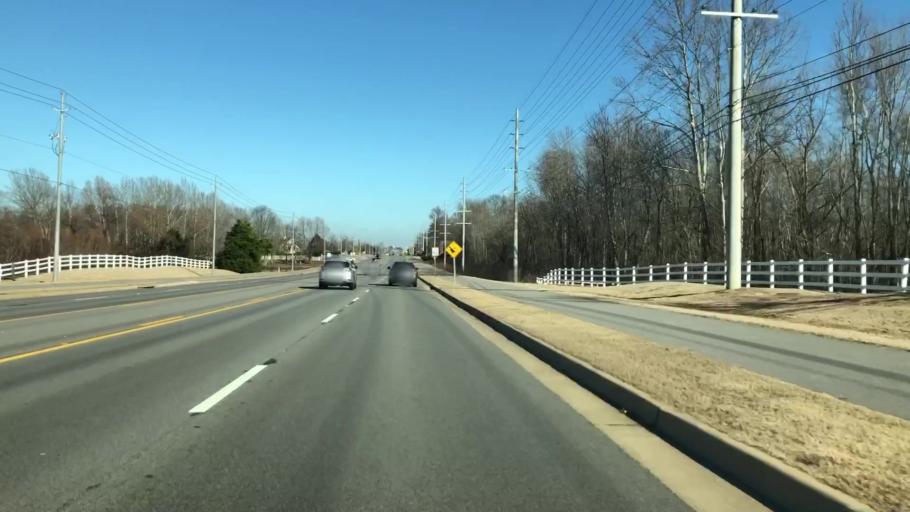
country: US
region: Alabama
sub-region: Madison County
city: Madison
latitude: 34.7135
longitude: -86.7864
